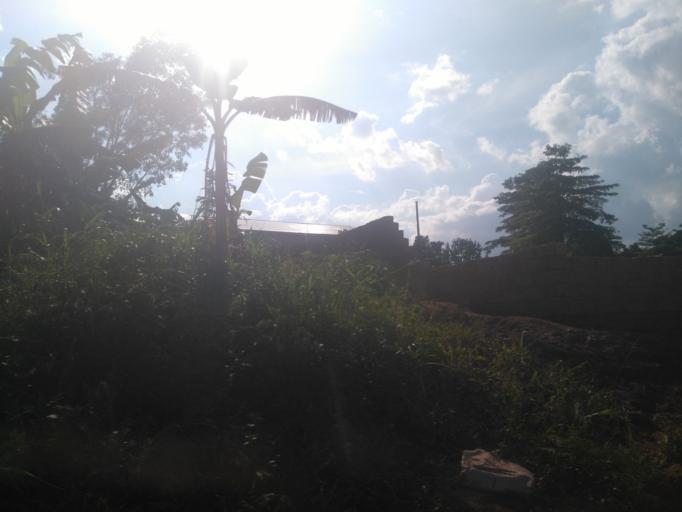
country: UG
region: Central Region
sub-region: Wakiso District
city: Wakiso
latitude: 0.3054
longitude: 32.4466
